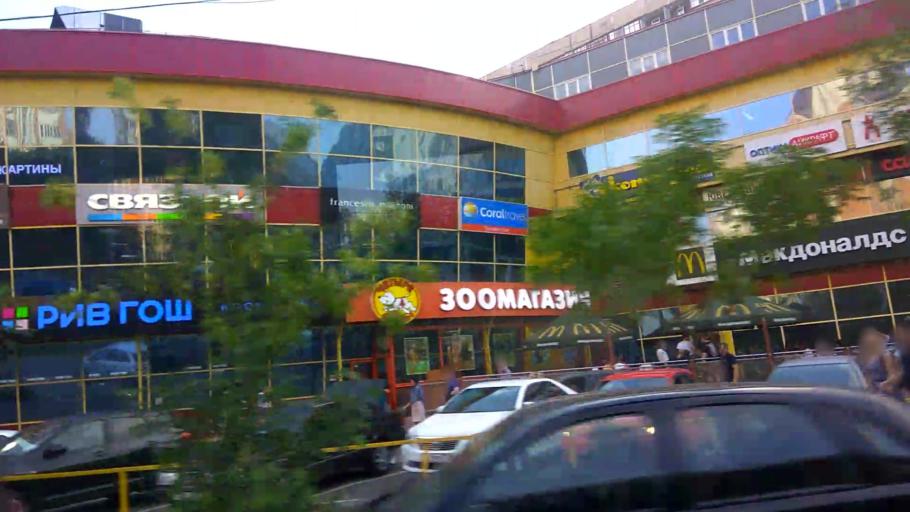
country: RU
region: Moskovskaya
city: Yubileyny
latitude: 55.9148
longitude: 37.8676
